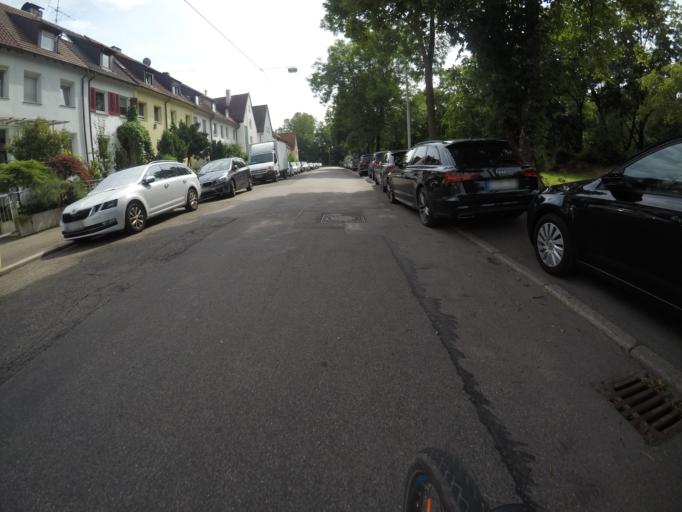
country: DE
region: Baden-Wuerttemberg
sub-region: Regierungsbezirk Stuttgart
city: Stuttgart-Ost
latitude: 48.7927
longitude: 9.1985
